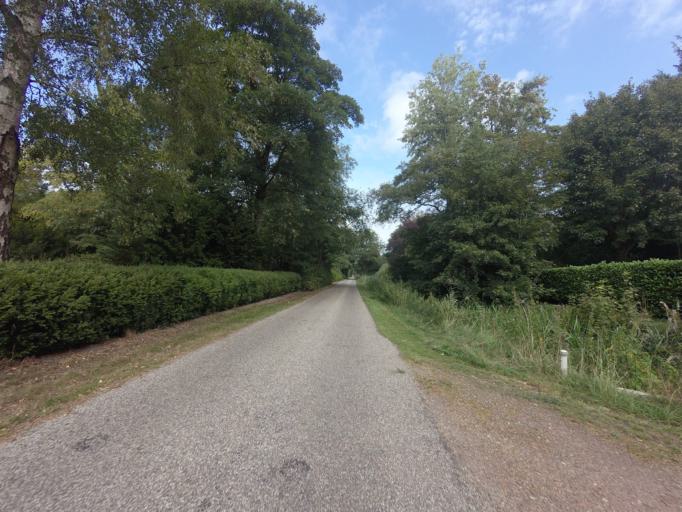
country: NL
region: Friesland
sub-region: Gemeente Heerenveen
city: Jubbega
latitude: 52.9885
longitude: 6.1129
